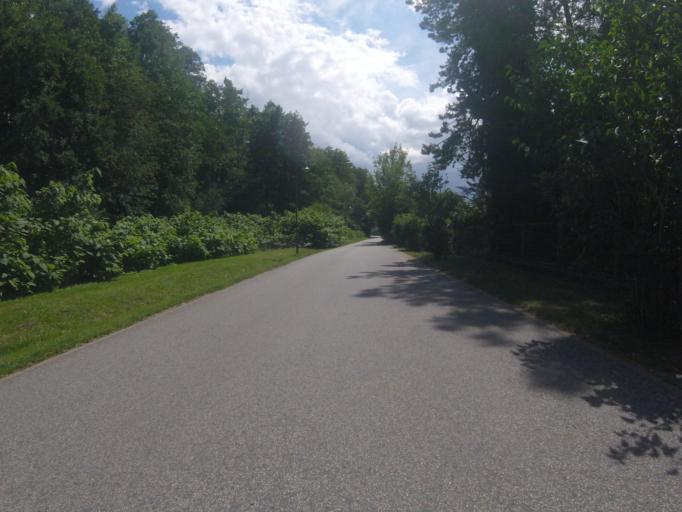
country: DE
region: Brandenburg
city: Bestensee
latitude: 52.2687
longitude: 13.6414
